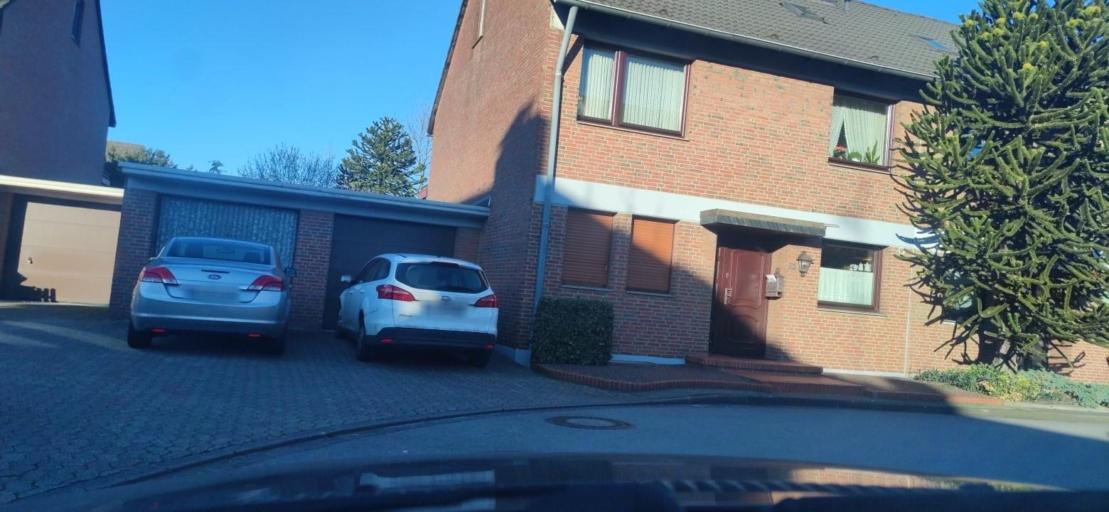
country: DE
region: North Rhine-Westphalia
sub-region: Regierungsbezirk Dusseldorf
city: Ratingen
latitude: 51.3088
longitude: 6.8236
